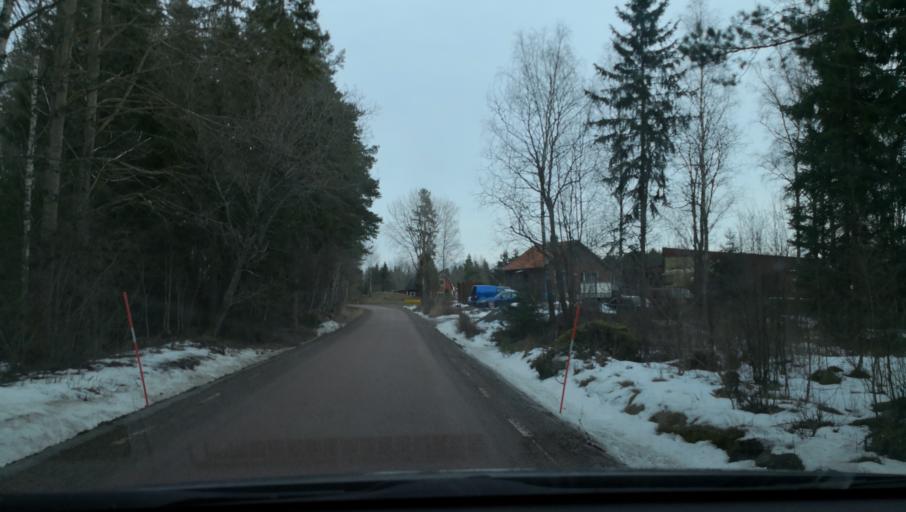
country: SE
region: Vaestmanland
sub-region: Vasteras
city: Skultuna
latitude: 59.6316
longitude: 16.4314
